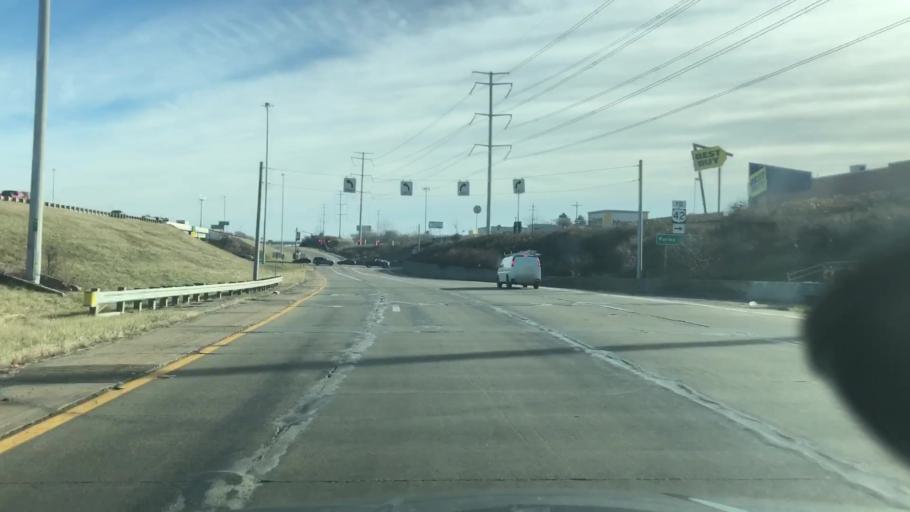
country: US
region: Ohio
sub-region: Cuyahoga County
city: Brooklyn
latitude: 41.4216
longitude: -81.7366
